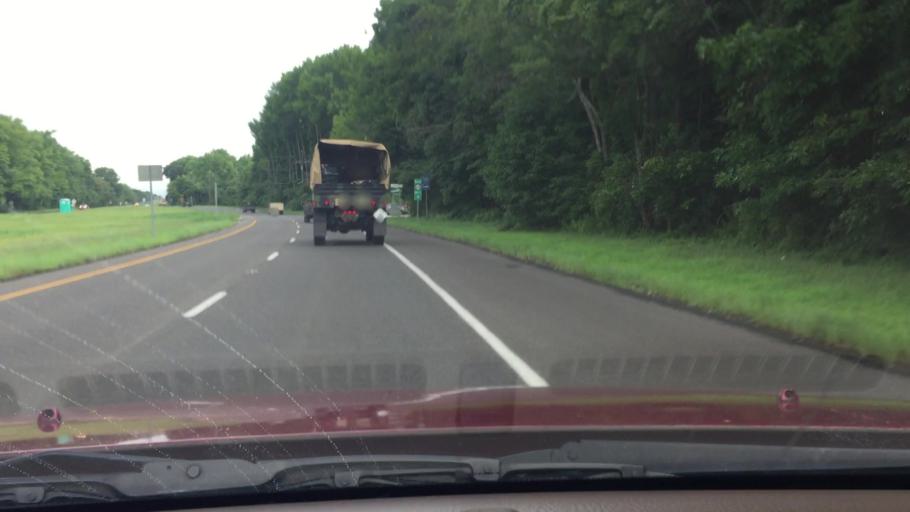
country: US
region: New Jersey
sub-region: Burlington County
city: Fort Dix
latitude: 40.0716
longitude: -74.6560
